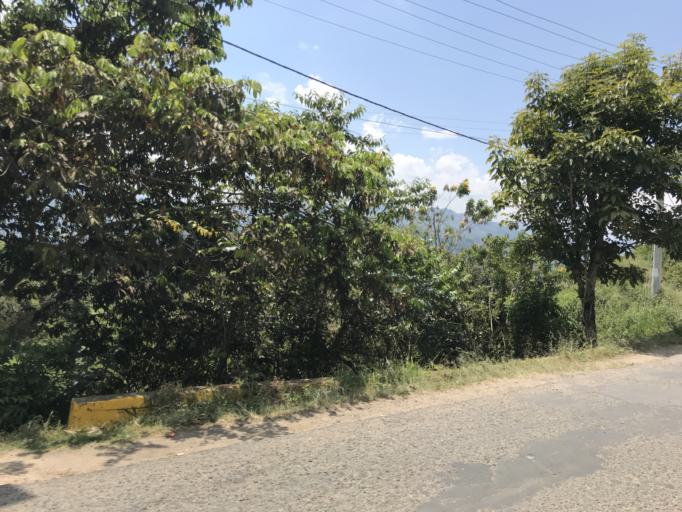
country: CO
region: Huila
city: San Agustin
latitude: 1.8765
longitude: -76.2575
